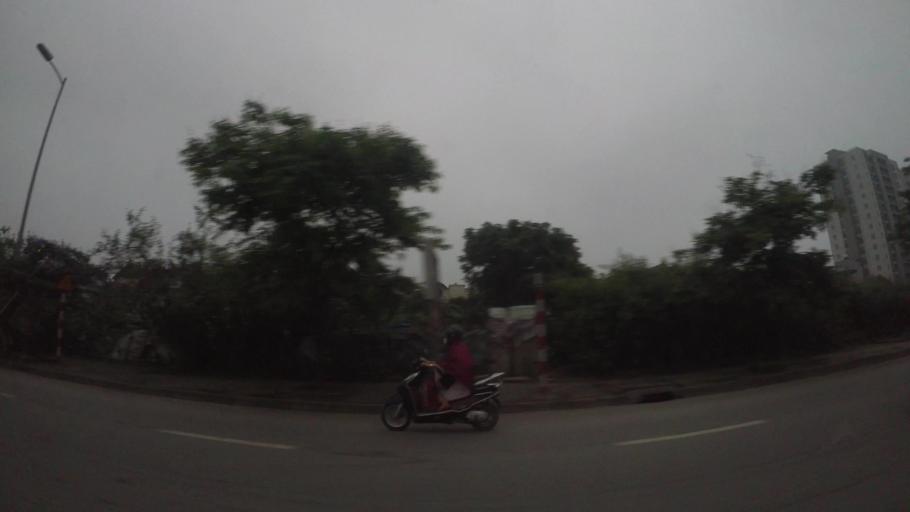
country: VN
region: Ha Noi
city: Van Dien
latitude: 20.9720
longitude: 105.8811
